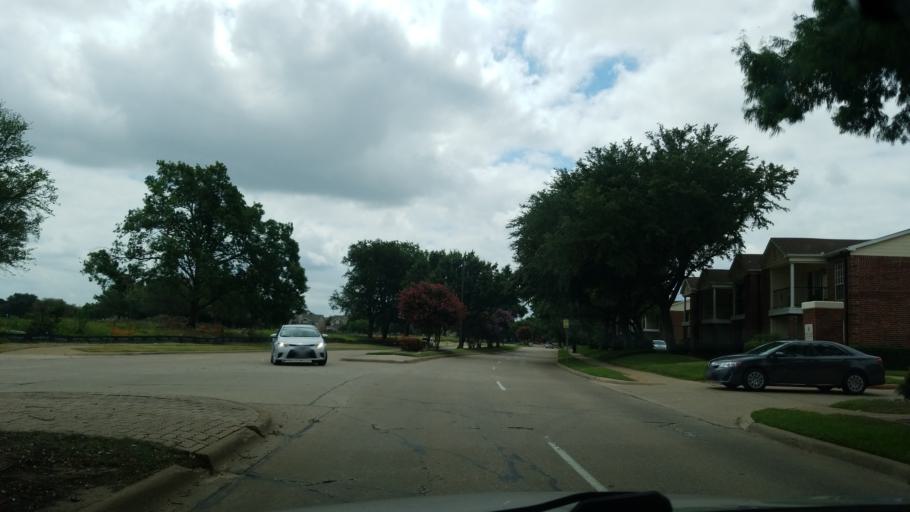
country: US
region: Texas
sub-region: Dallas County
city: Farmers Branch
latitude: 32.9400
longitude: -96.9495
